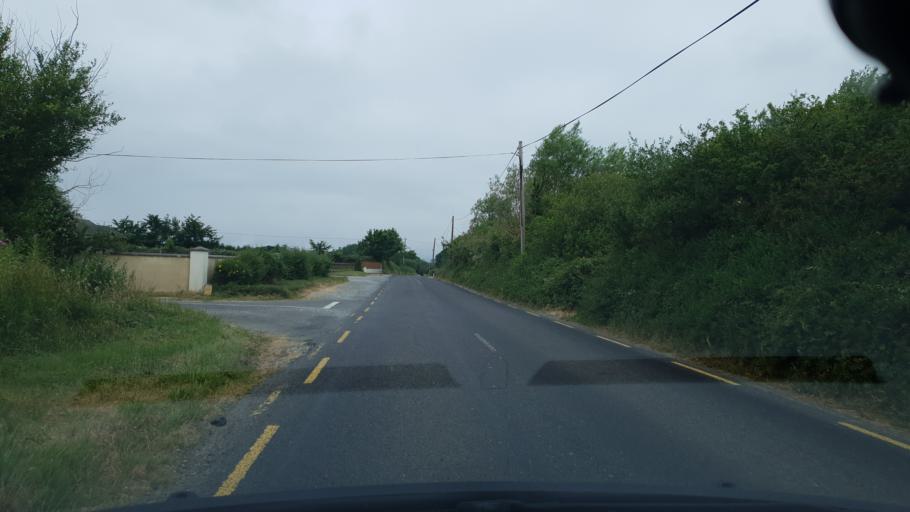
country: IE
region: Munster
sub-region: Ciarrai
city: Tralee
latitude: 52.1636
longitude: -9.6267
